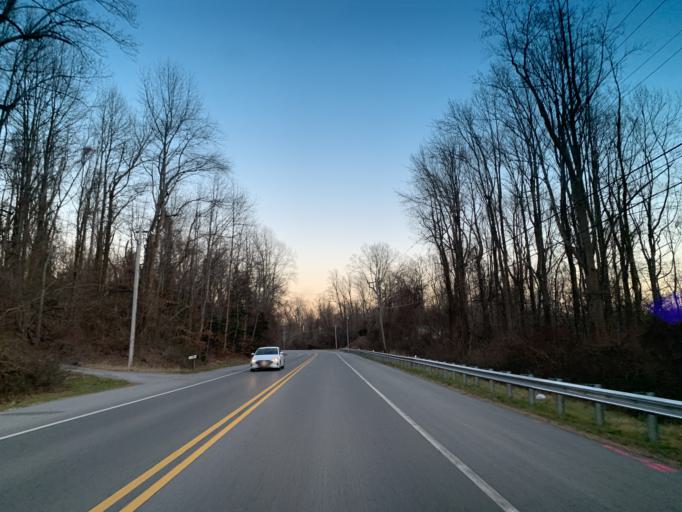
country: US
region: Maryland
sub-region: Calvert County
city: Prince Frederick
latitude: 38.5569
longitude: -76.5284
